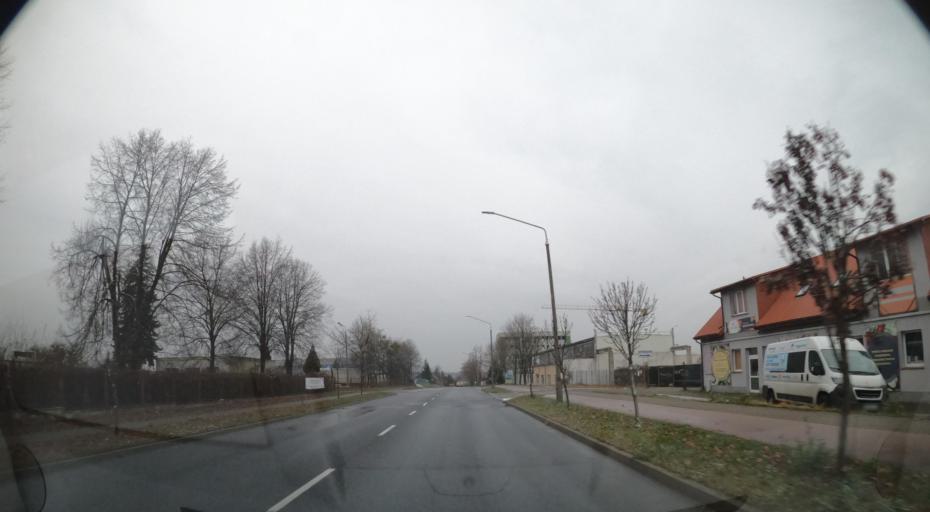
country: PL
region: Masovian Voivodeship
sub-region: Powiat radomski
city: Trablice
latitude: 51.3807
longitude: 21.1230
